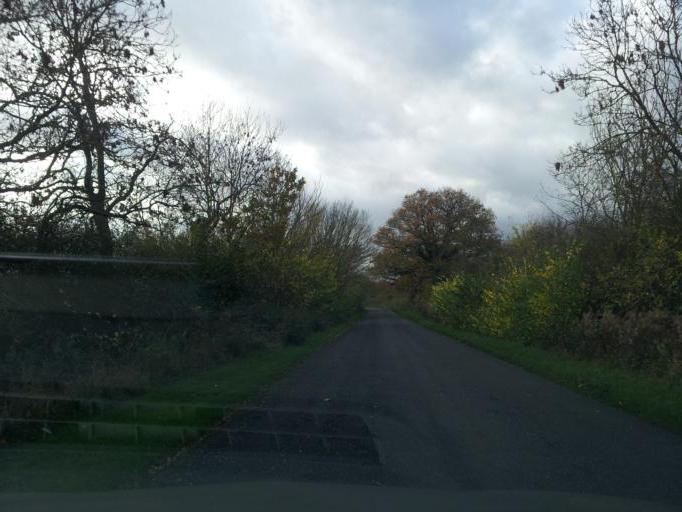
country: GB
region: England
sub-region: Lincolnshire
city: Long Bennington
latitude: 52.9844
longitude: -0.7810
